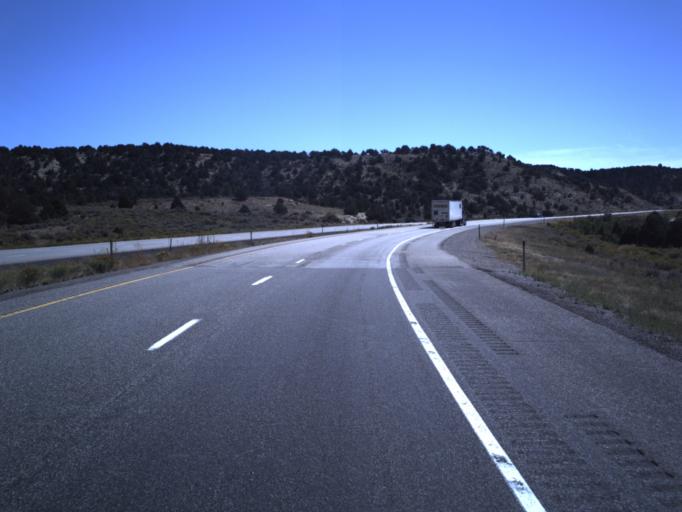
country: US
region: Utah
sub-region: Sevier County
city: Salina
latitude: 38.8019
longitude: -111.5182
